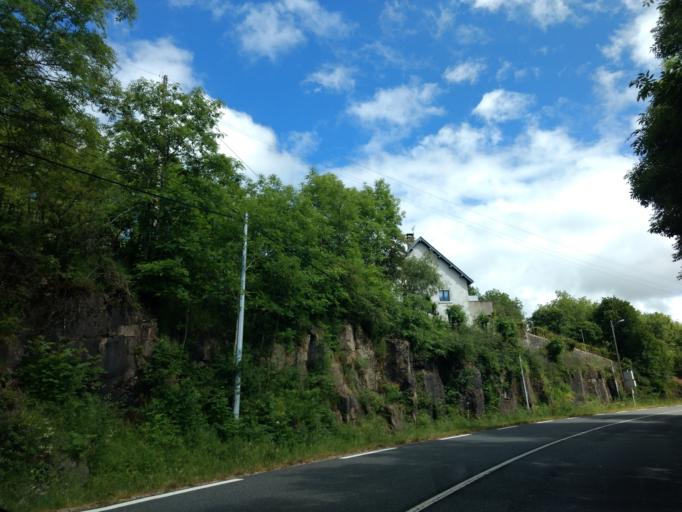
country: FR
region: Midi-Pyrenees
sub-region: Departement de l'Aveyron
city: Laguiole
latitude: 44.6783
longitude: 2.8509
